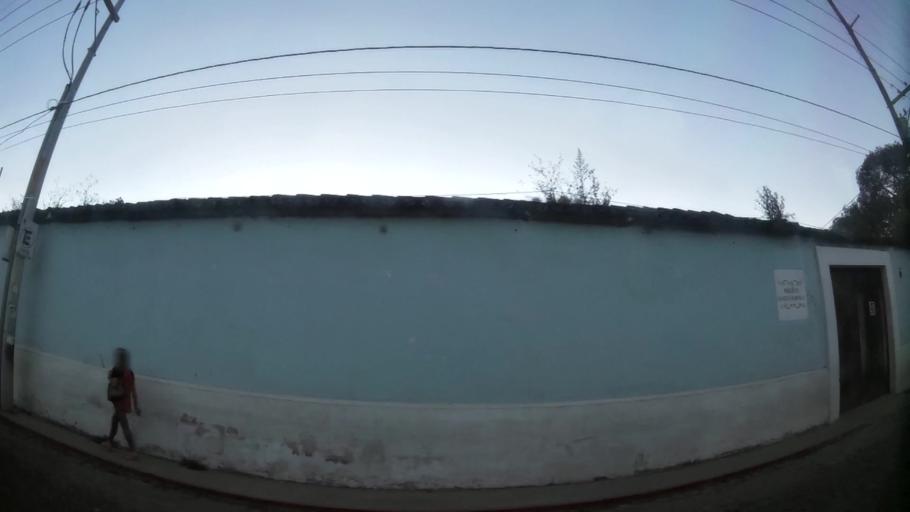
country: GT
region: Sacatepequez
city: Antigua Guatemala
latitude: 14.5595
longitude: -90.7266
